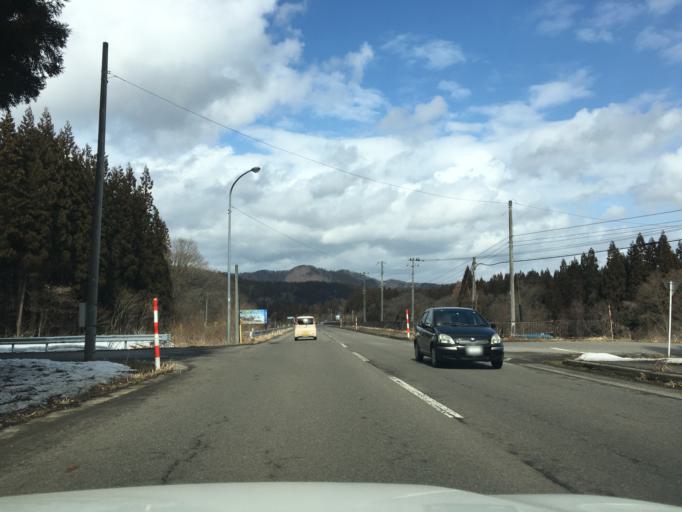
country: JP
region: Akita
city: Takanosu
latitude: 40.0225
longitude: 140.2746
